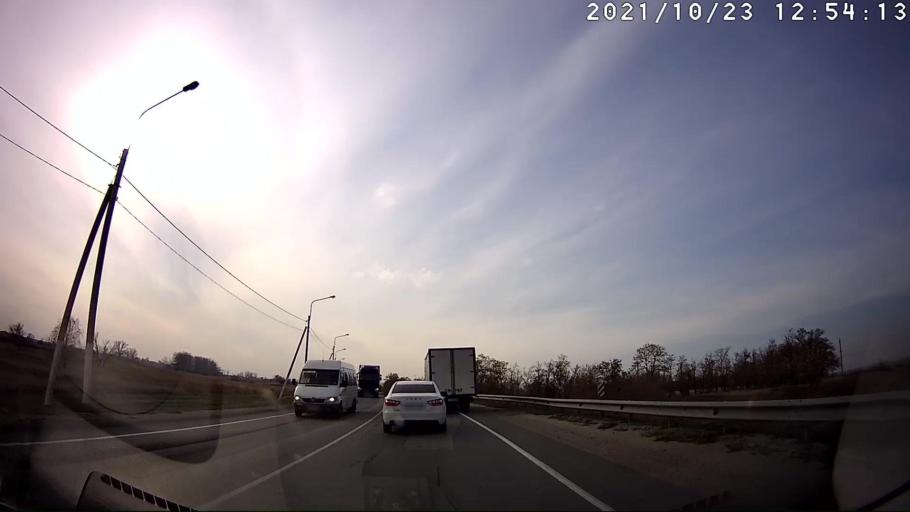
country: RU
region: Volgograd
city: Dubovka
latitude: 49.0578
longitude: 44.8032
